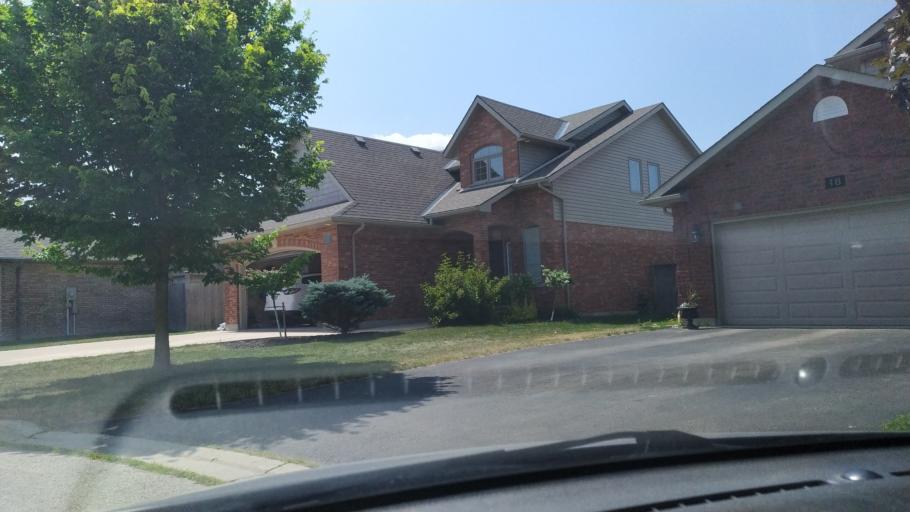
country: CA
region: Ontario
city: Stratford
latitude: 43.3643
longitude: -81.0031
